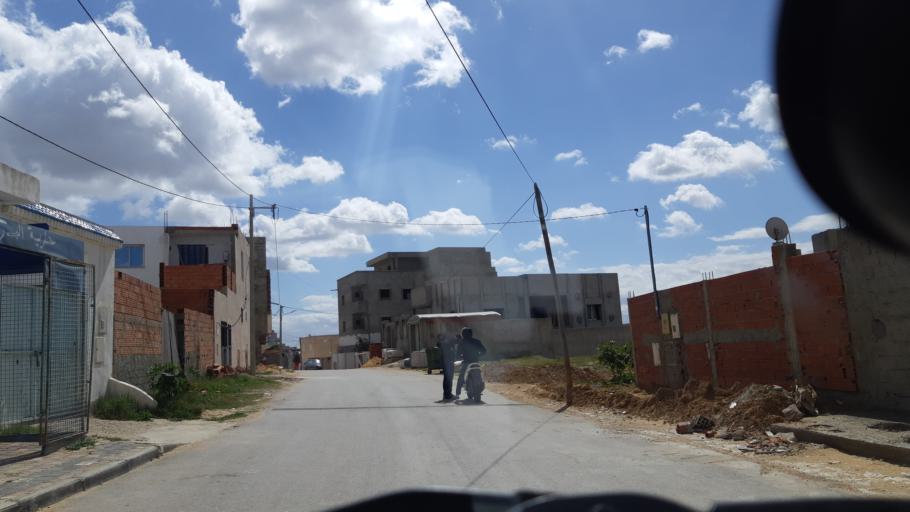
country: TN
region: Susah
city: Akouda
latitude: 35.8798
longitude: 10.5408
